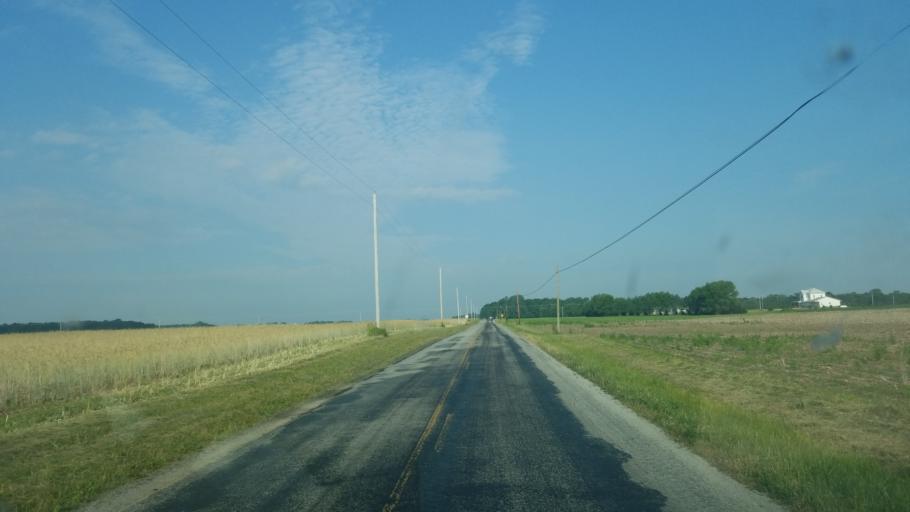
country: US
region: Ohio
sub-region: Hardin County
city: Kenton
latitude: 40.6223
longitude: -83.7145
